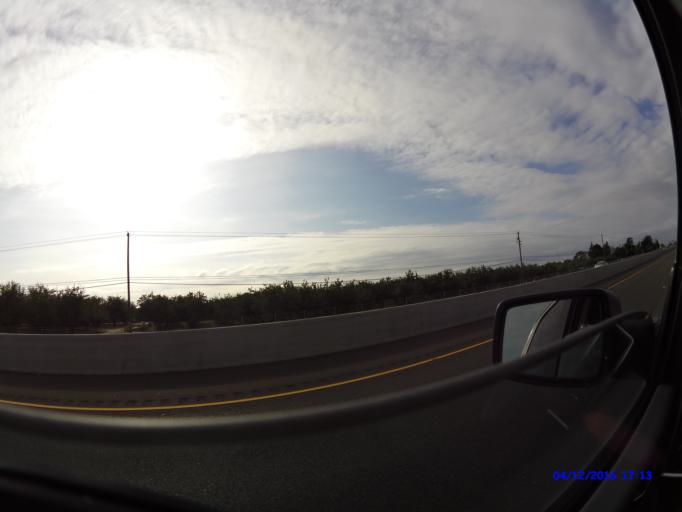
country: US
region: California
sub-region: San Joaquin County
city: Manteca
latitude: 37.8410
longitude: -121.2178
